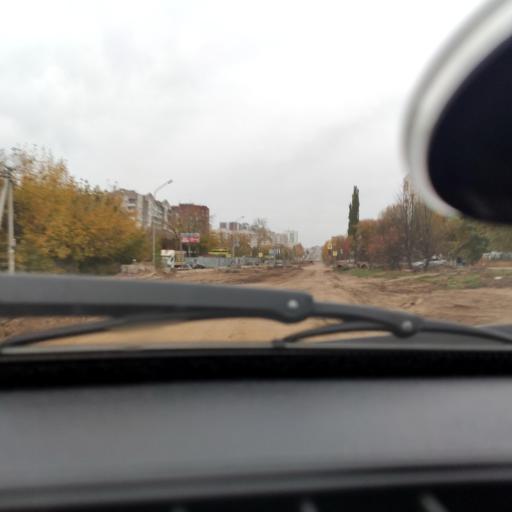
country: RU
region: Bashkortostan
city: Ufa
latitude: 54.7478
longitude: 56.0011
